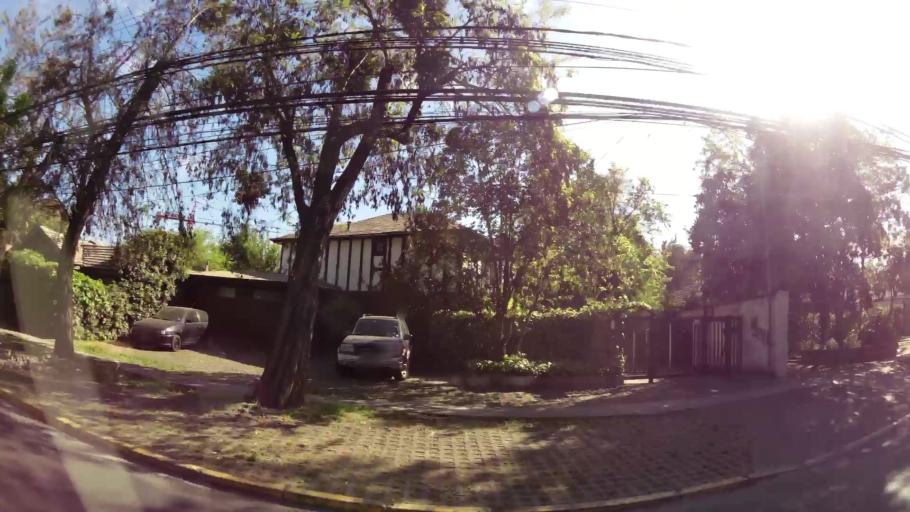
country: CL
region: Santiago Metropolitan
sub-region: Provincia de Santiago
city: Villa Presidente Frei, Nunoa, Santiago, Chile
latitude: -33.4384
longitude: -70.5653
